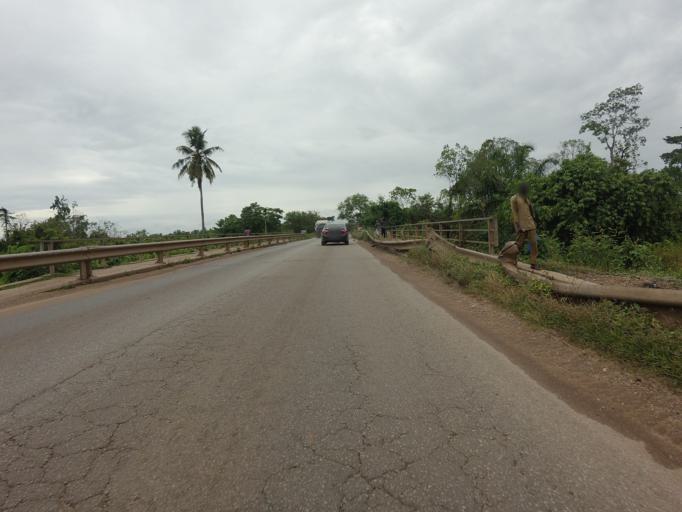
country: GH
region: Eastern
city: Begoro
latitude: 6.3861
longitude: -0.5526
